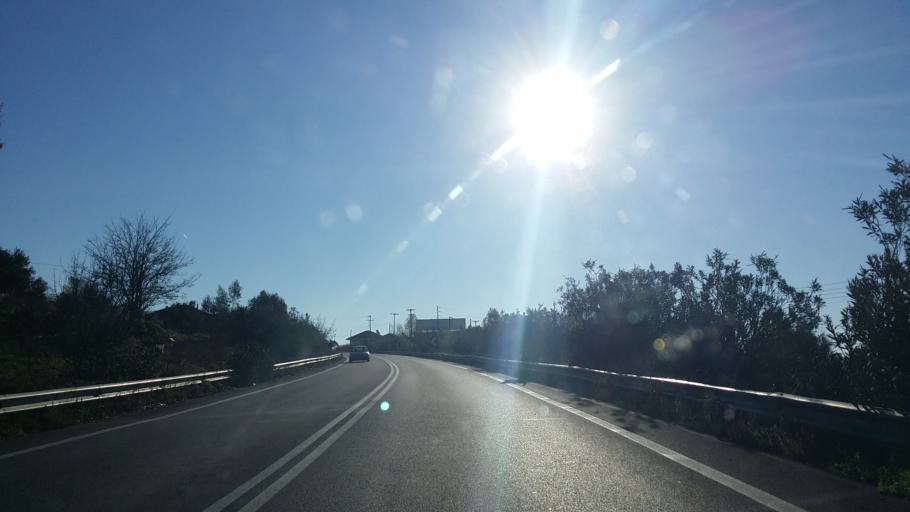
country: GR
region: West Greece
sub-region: Nomos Aitolias kai Akarnanias
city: Fitiai
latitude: 38.6906
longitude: 21.2266
